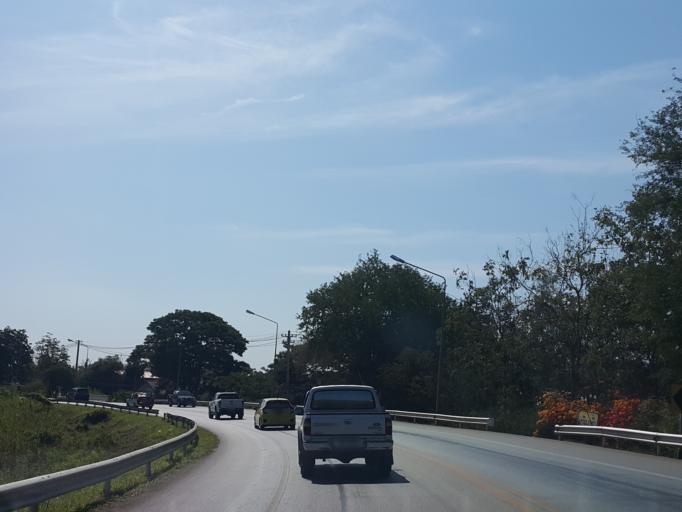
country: TH
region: Sukhothai
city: Sawankhalok
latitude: 17.2719
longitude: 99.8400
